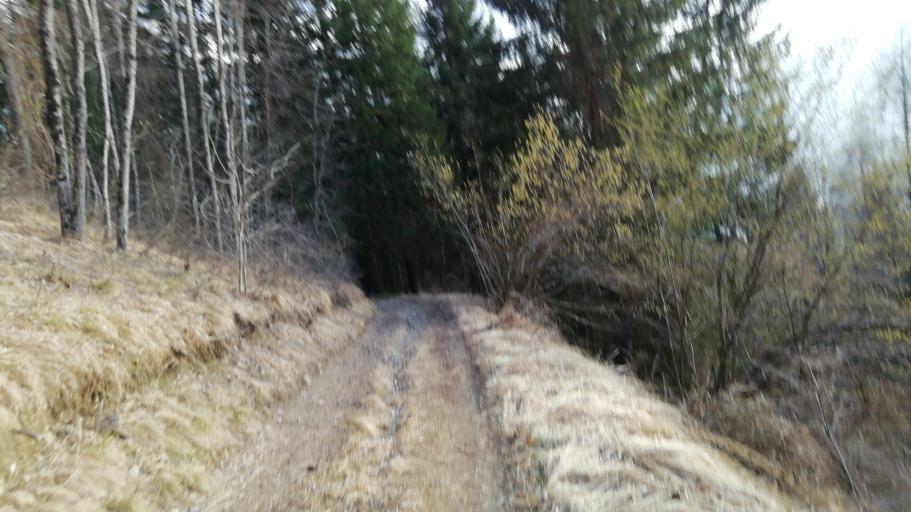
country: IT
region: Veneto
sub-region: Provincia di Belluno
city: Valle di Cadore
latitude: 46.4203
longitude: 12.3173
